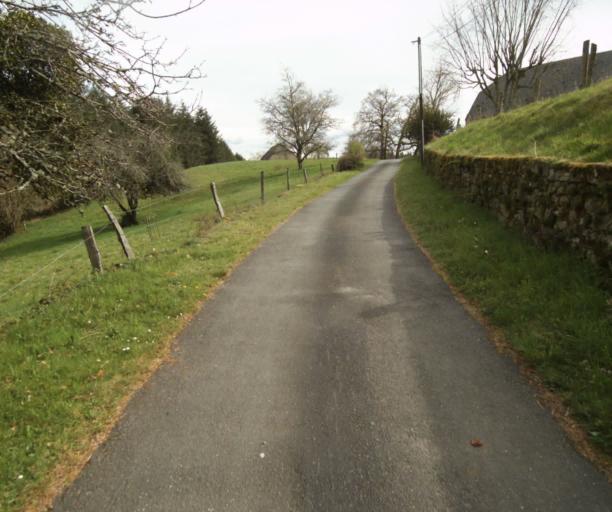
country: FR
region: Limousin
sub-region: Departement de la Correze
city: Argentat
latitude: 45.2033
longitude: 1.9684
